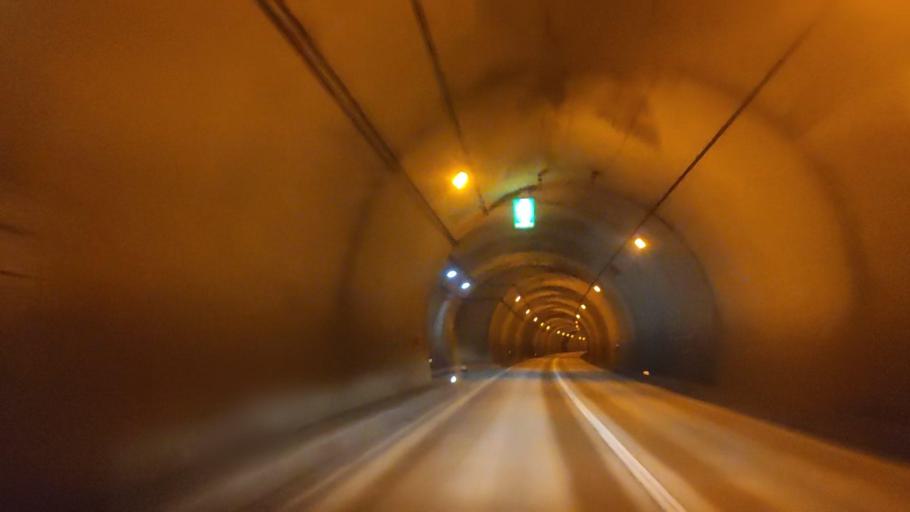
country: JP
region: Tottori
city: Kurayoshi
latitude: 35.3147
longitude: 133.7543
